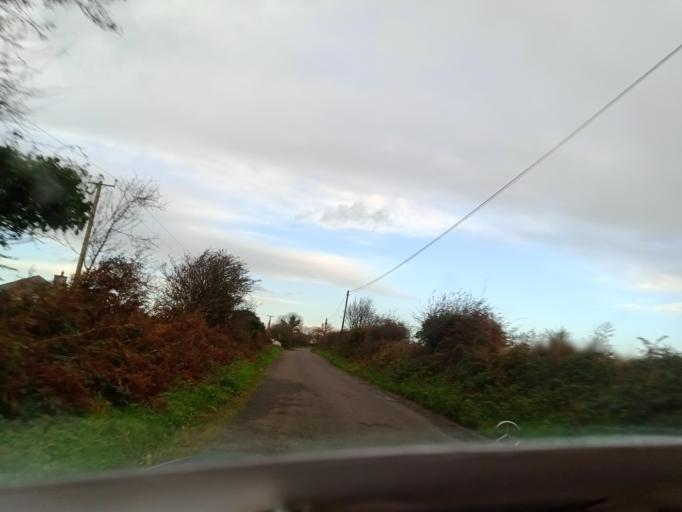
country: IE
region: Munster
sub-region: Waterford
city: Waterford
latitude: 52.3173
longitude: -7.0455
